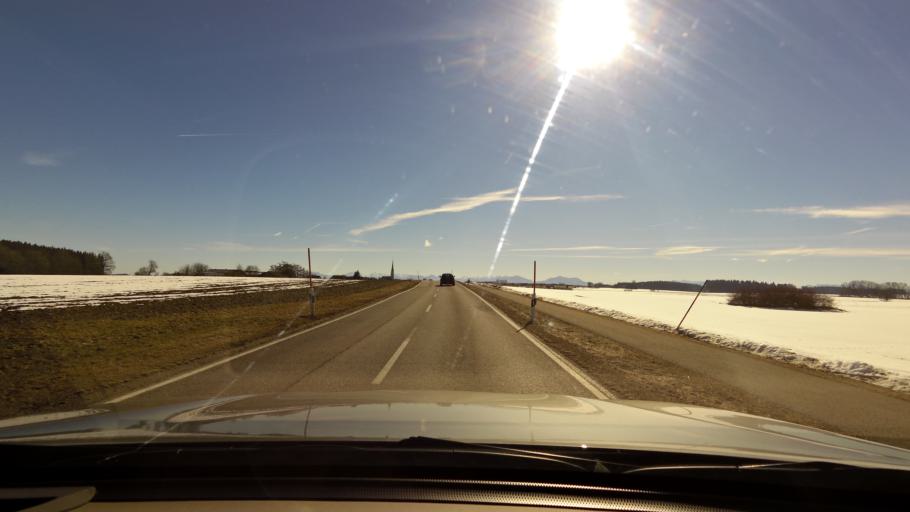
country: DE
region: Bavaria
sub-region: Upper Bavaria
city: Kienberg
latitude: 48.0805
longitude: 12.4820
